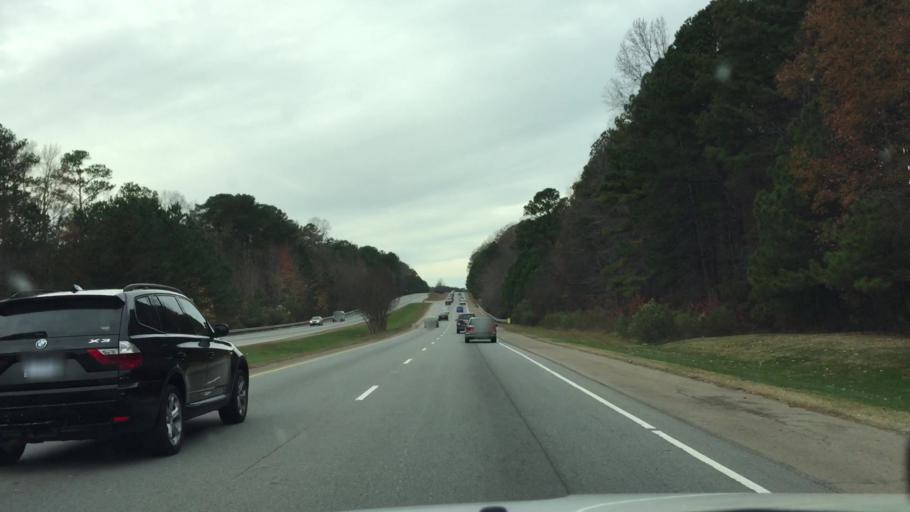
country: US
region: North Carolina
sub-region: Wake County
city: Apex
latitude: 35.7418
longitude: -78.8103
